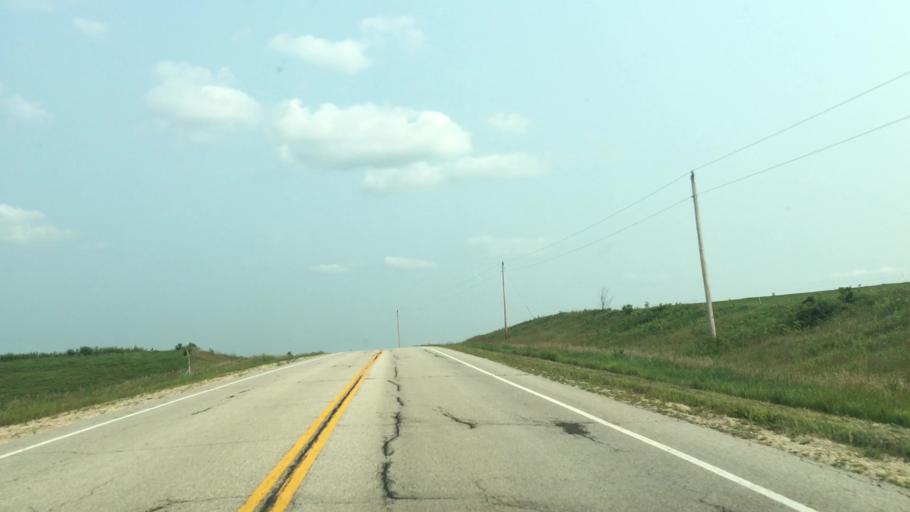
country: US
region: Minnesota
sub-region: Fillmore County
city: Preston
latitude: 43.6905
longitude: -91.9470
